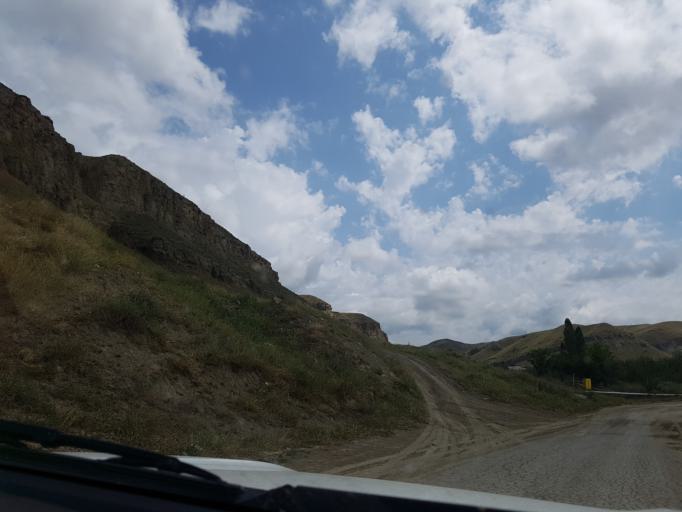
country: TM
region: Ahal
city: Baharly
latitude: 38.2232
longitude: 56.8916
